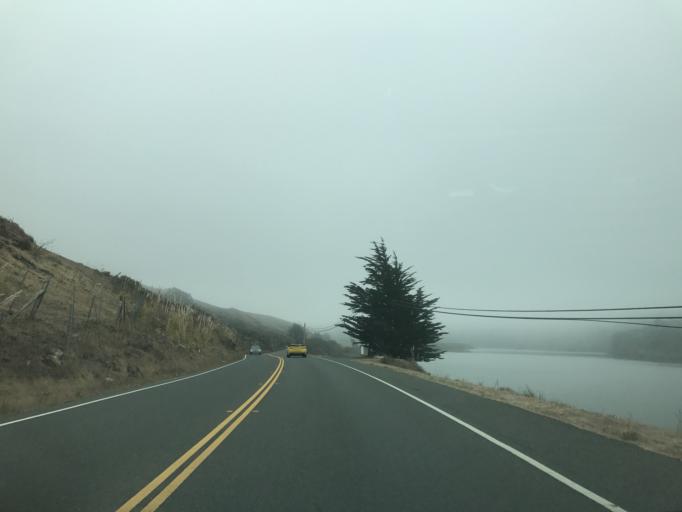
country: US
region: California
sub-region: Sonoma County
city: Monte Rio
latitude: 38.4464
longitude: -123.1125
